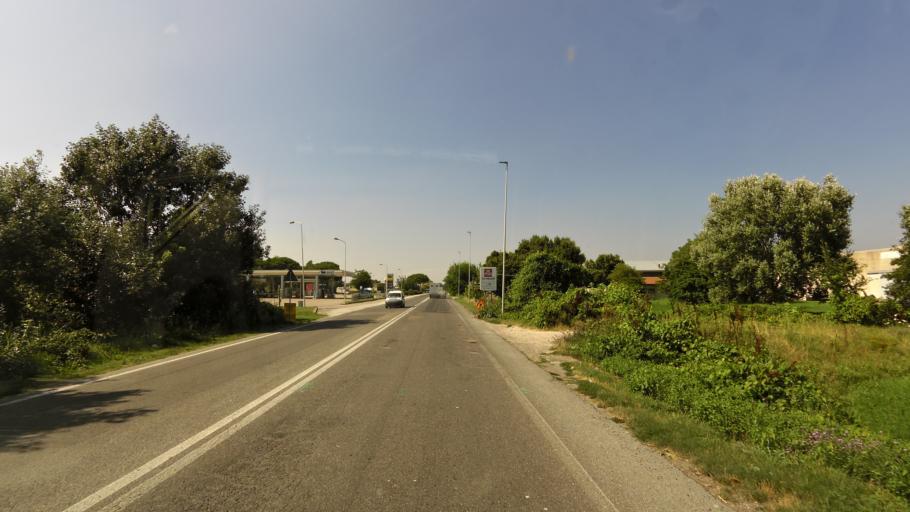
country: IT
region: Emilia-Romagna
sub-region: Provincia di Ravenna
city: Ravenna
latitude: 44.4367
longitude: 12.2124
